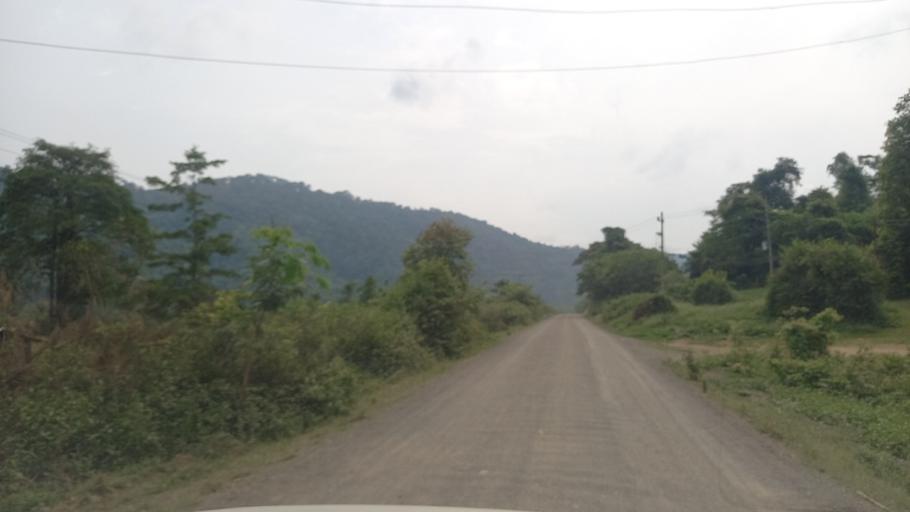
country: LA
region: Bolikhamxai
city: Ban Nahin
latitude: 18.1495
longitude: 104.7407
